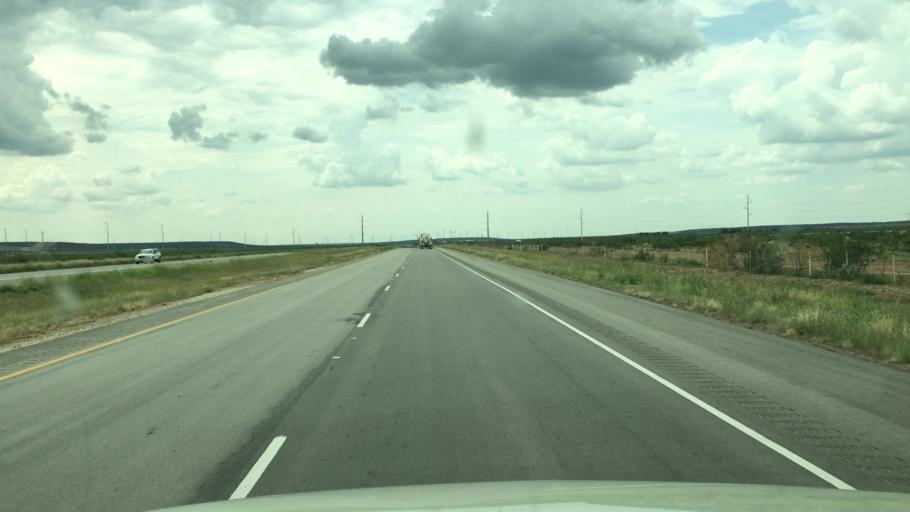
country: US
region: Texas
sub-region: Sterling County
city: Sterling City
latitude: 31.9580
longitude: -101.2037
